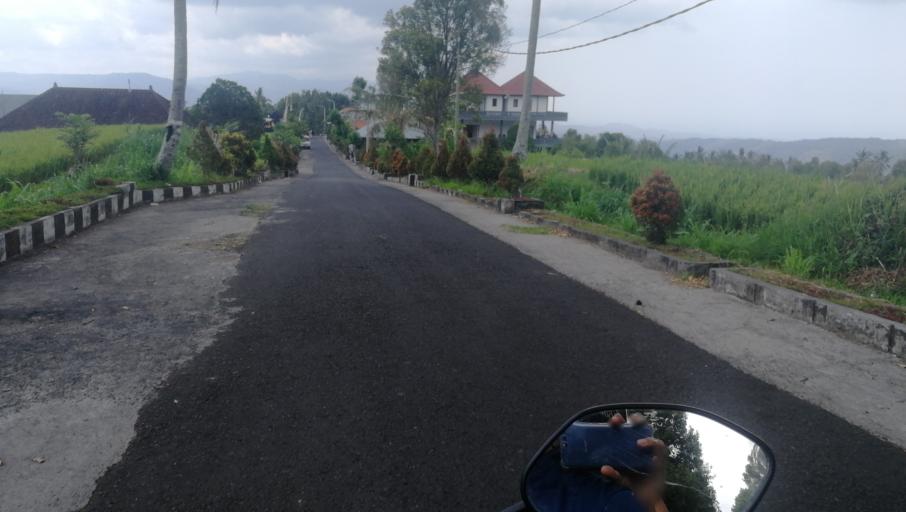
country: ID
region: Bali
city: Munduk
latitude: -8.2793
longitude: 115.0378
